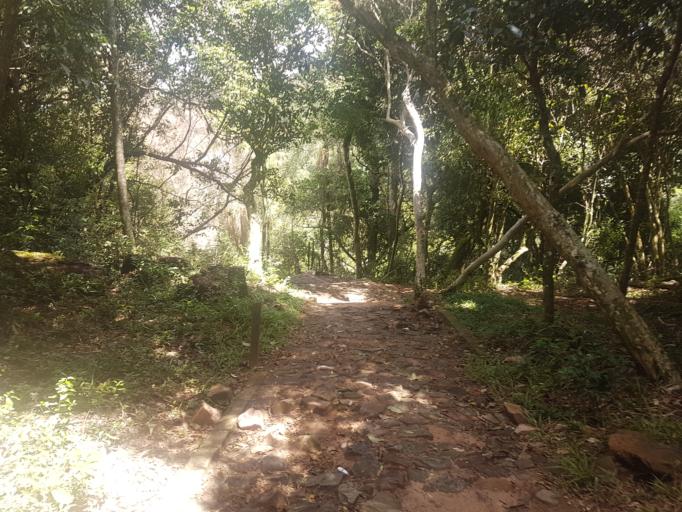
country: PY
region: Paraguari
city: La Colmena
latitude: -25.9778
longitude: -56.7292
